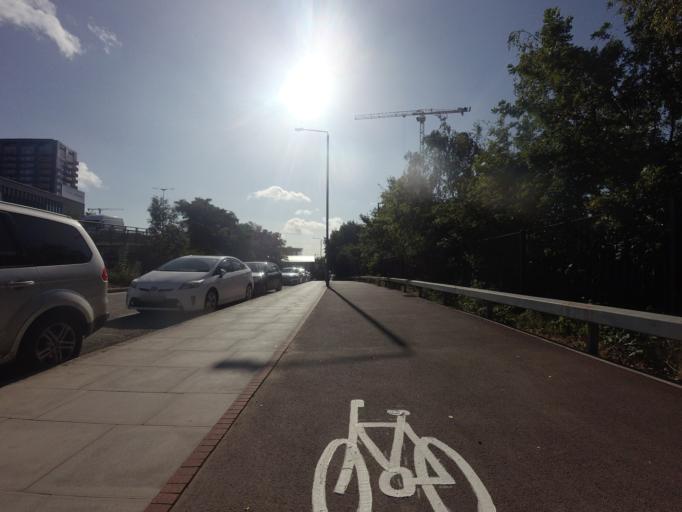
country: GB
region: England
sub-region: Greater London
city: Poplar
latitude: 51.5097
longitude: 0.0035
